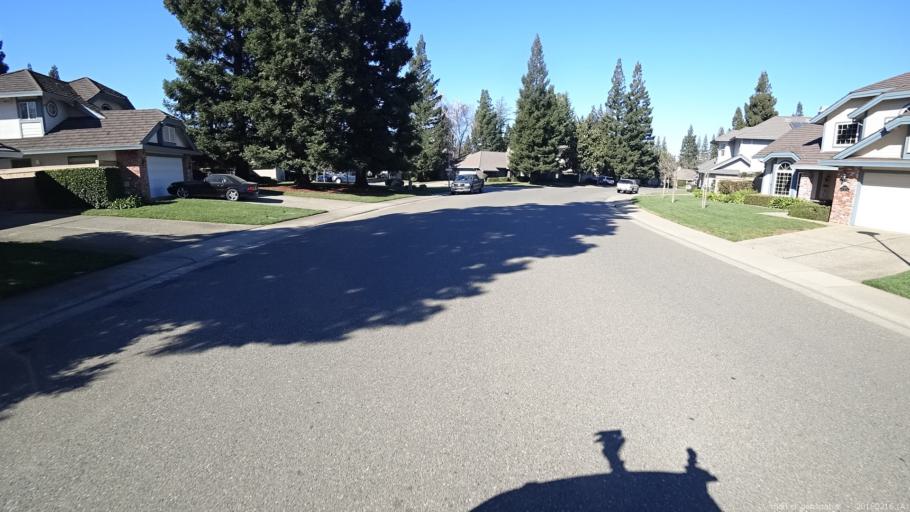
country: US
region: California
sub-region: Sacramento County
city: Gold River
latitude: 38.6203
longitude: -121.2530
